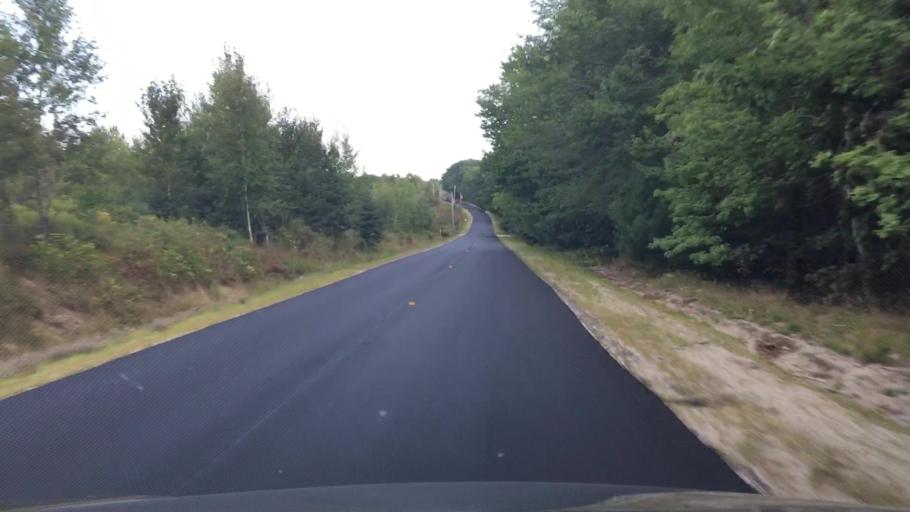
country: US
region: Maine
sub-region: Hancock County
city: Penobscot
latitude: 44.5409
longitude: -68.6163
